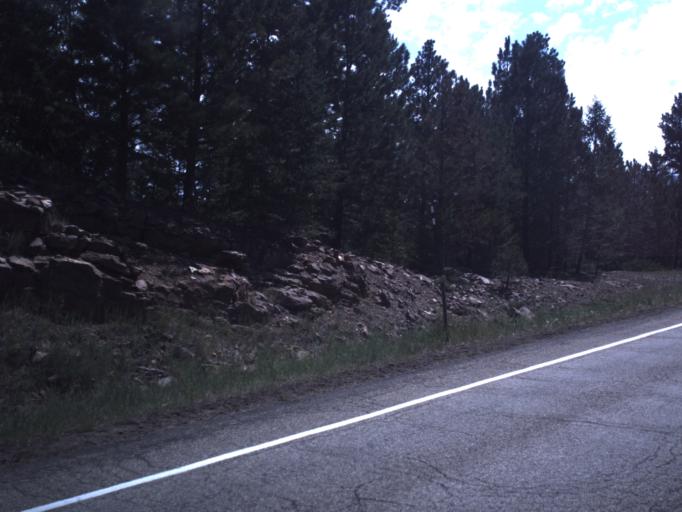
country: US
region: Utah
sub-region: Daggett County
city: Manila
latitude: 40.8481
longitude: -109.6685
